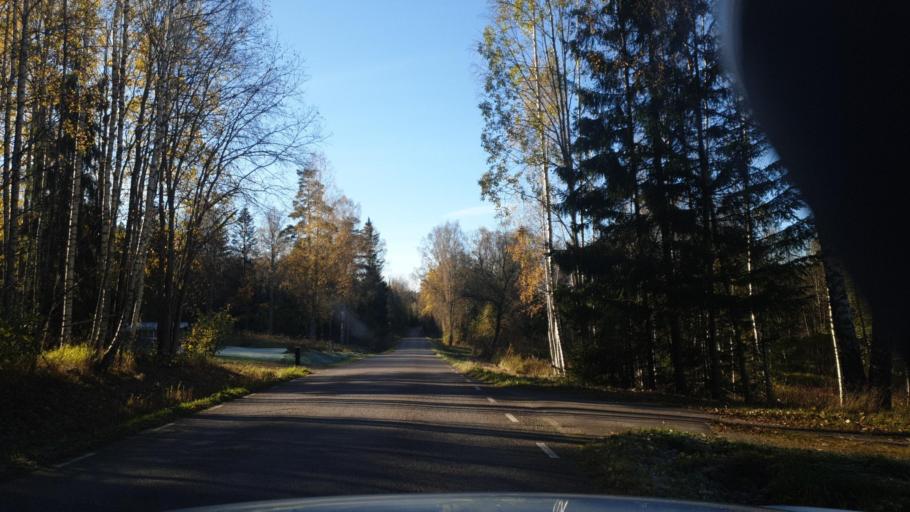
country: SE
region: Vaermland
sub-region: Grums Kommun
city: Grums
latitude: 59.4167
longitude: 13.0833
